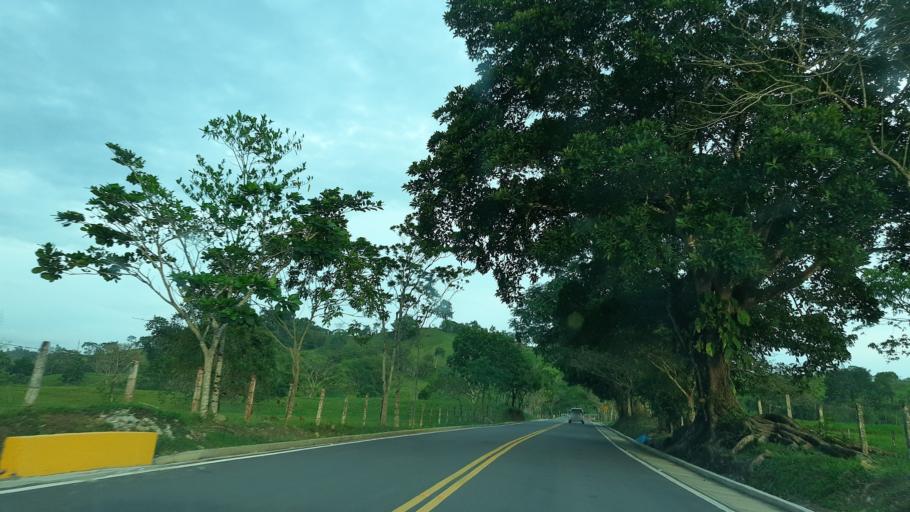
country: CO
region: Casanare
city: Sabanalarga
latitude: 4.7956
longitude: -73.0563
